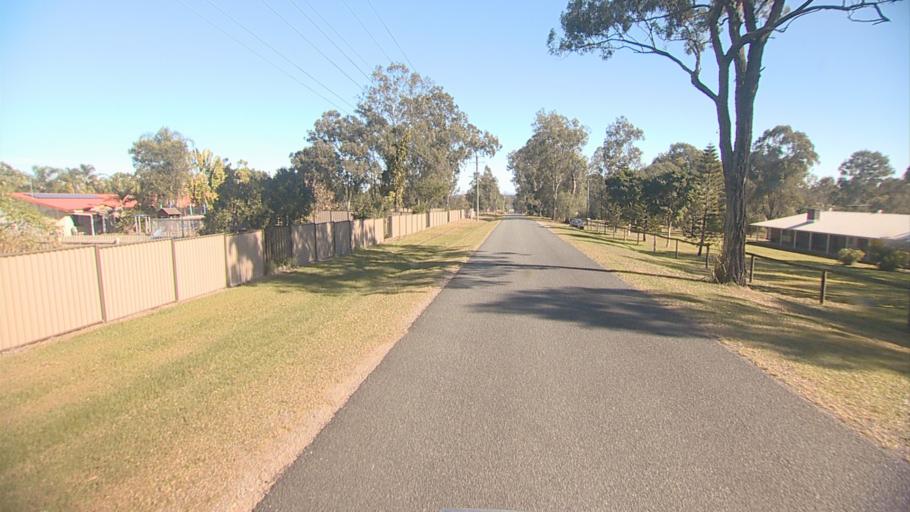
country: AU
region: Queensland
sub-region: Logan
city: Windaroo
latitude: -27.7848
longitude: 153.1447
